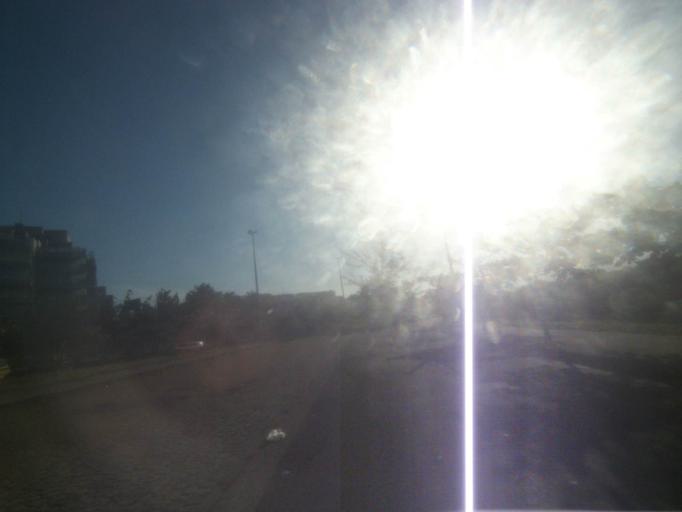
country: BR
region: Rio de Janeiro
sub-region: Nilopolis
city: Nilopolis
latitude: -23.0220
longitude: -43.4483
